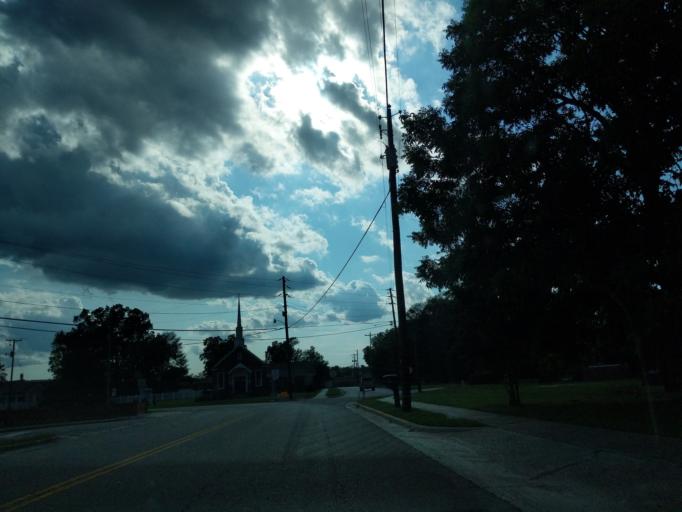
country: US
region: South Carolina
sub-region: Barnwell County
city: Williston
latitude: 33.4029
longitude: -81.4197
